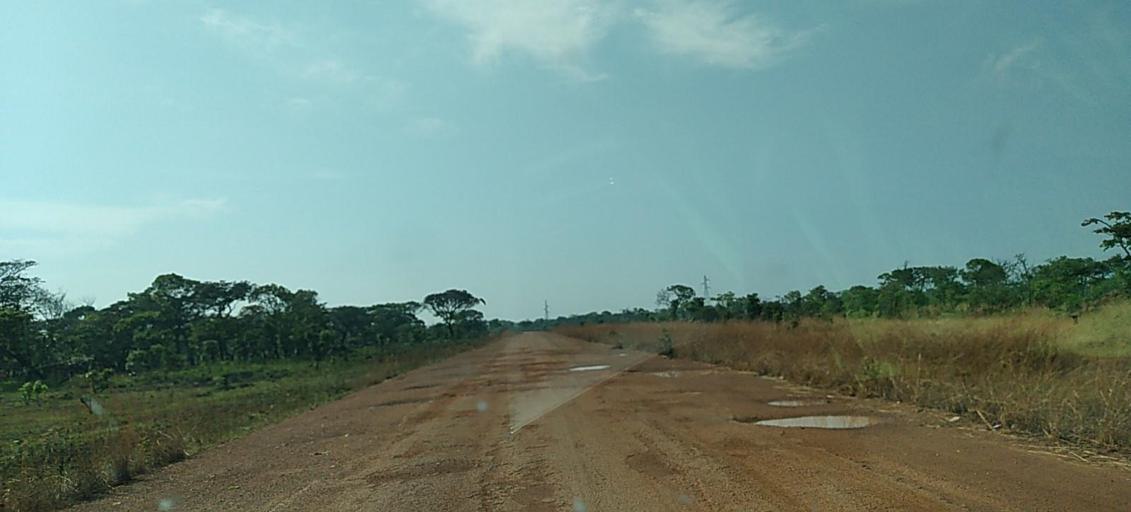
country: ZM
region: North-Western
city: Mwinilunga
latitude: -11.7817
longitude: 25.0239
